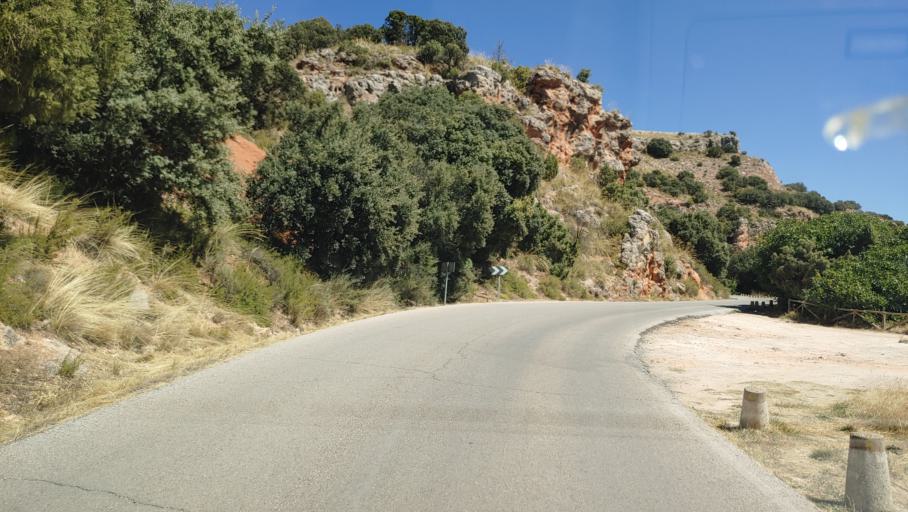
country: ES
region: Castille-La Mancha
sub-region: Provincia de Ciudad Real
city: Ruidera
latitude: 38.9410
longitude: -2.8509
